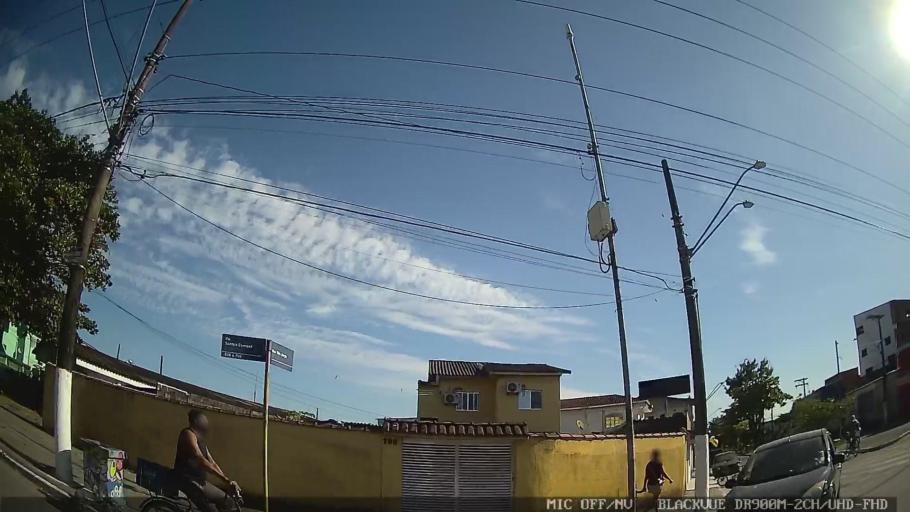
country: BR
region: Sao Paulo
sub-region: Santos
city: Santos
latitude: -23.9494
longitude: -46.2956
